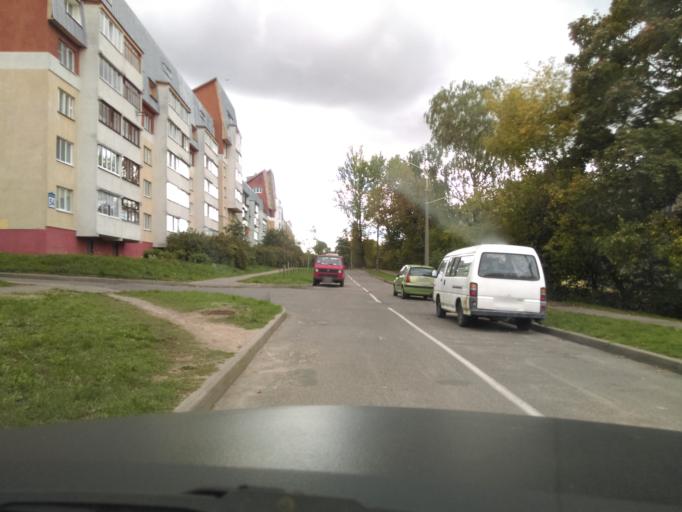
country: BY
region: Minsk
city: Minsk
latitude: 53.9113
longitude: 27.6304
